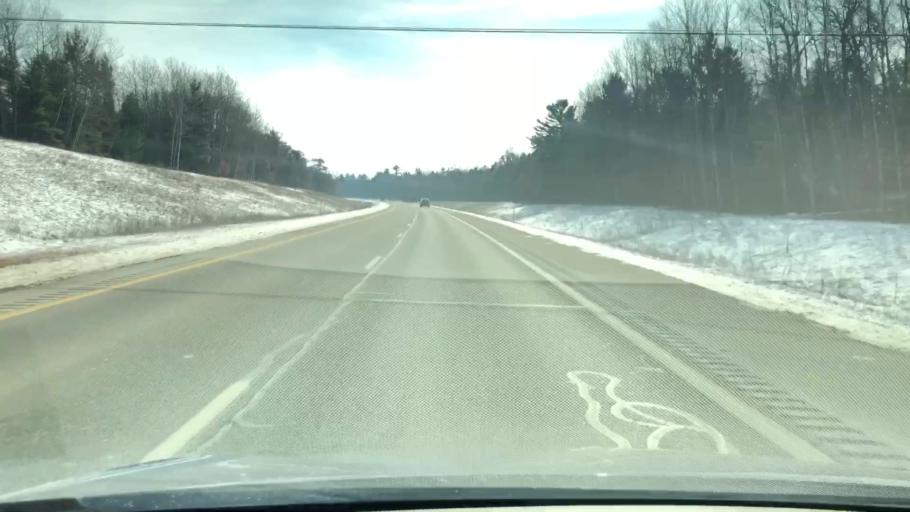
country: US
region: Michigan
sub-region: Crawford County
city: Grayling
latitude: 44.5545
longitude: -84.7061
